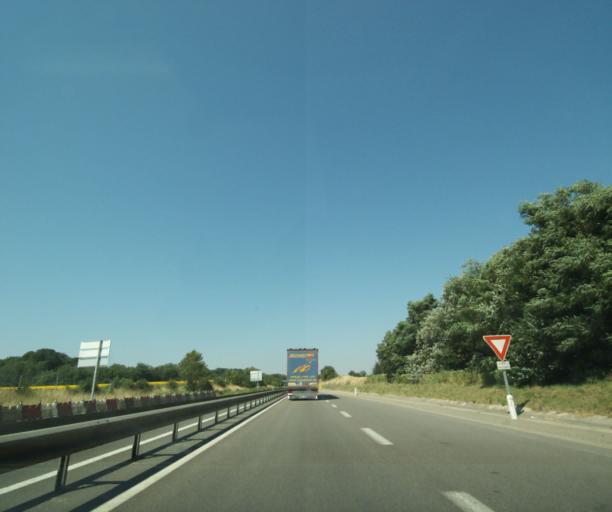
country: FR
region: Champagne-Ardenne
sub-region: Departement de la Haute-Marne
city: Saint-Dizier
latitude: 48.6210
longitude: 4.9586
